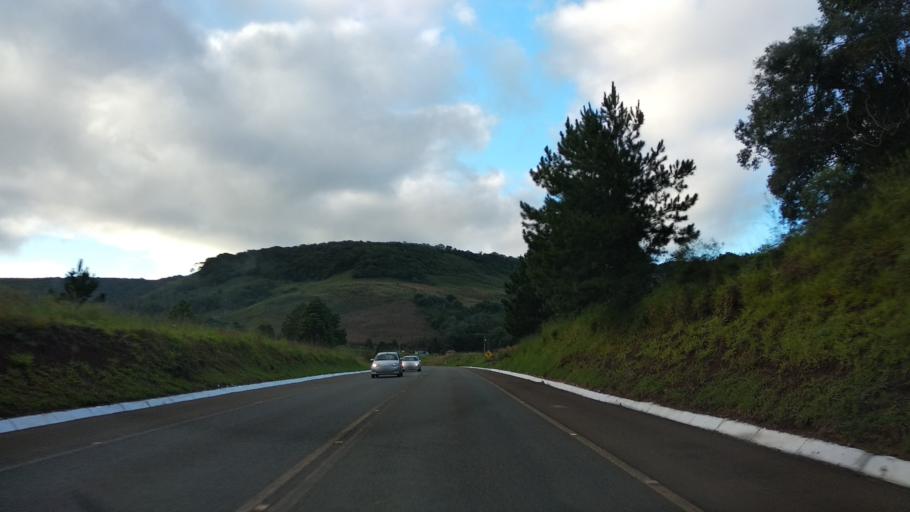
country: BR
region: Santa Catarina
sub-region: Curitibanos
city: Curitibanos
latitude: -27.5729
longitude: -50.8076
